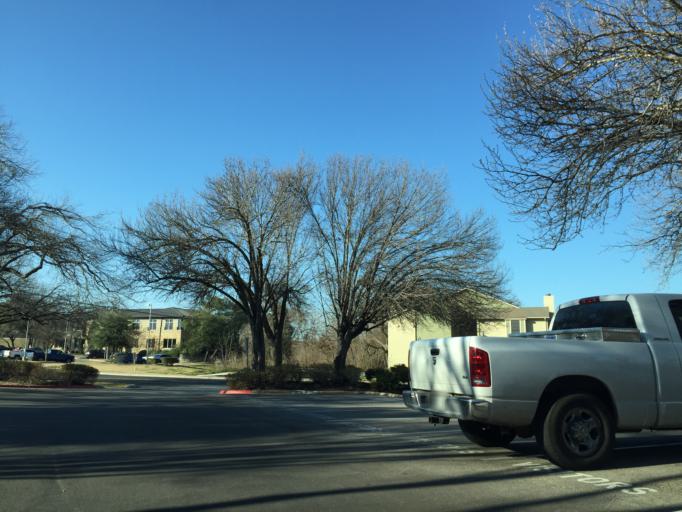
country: US
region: Texas
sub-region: Williamson County
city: Jollyville
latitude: 30.4376
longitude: -97.7674
